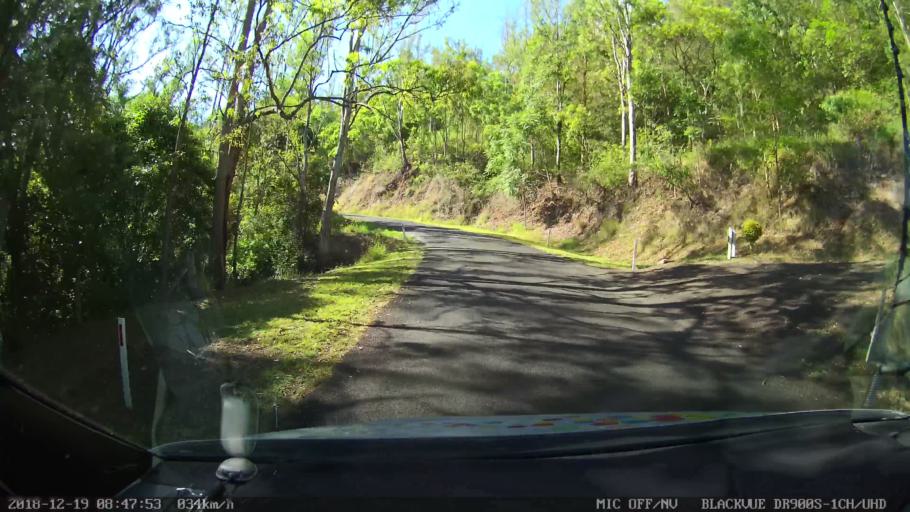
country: AU
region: New South Wales
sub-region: Kyogle
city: Kyogle
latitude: -28.3693
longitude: 152.9710
